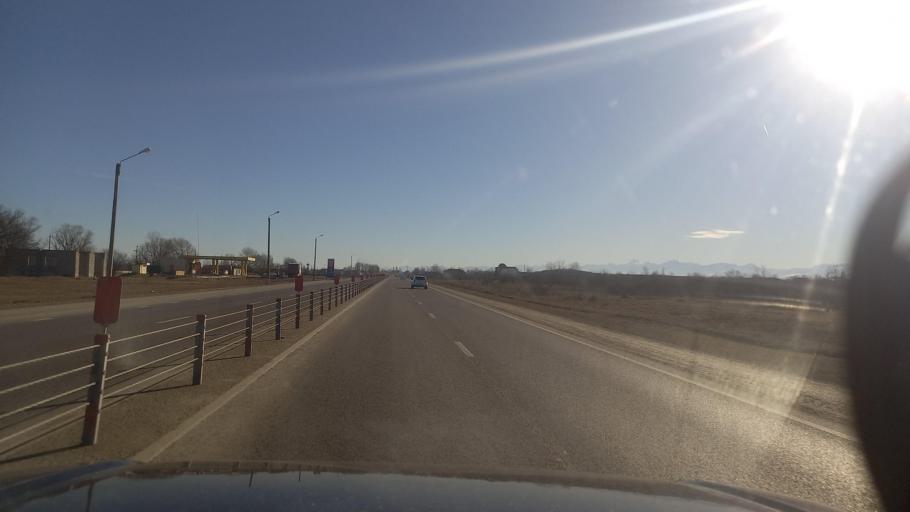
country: RU
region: Kabardino-Balkariya
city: Staryy Cherek
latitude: 43.4779
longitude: 43.8217
